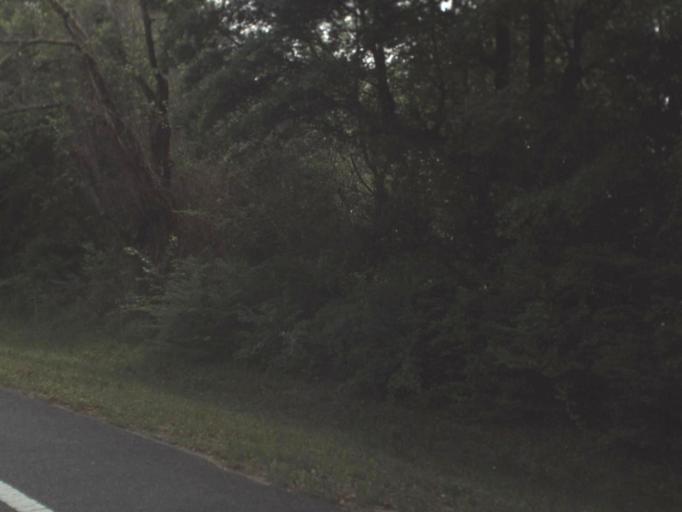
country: US
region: Florida
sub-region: Santa Rosa County
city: Point Baker
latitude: 30.7373
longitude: -87.0936
